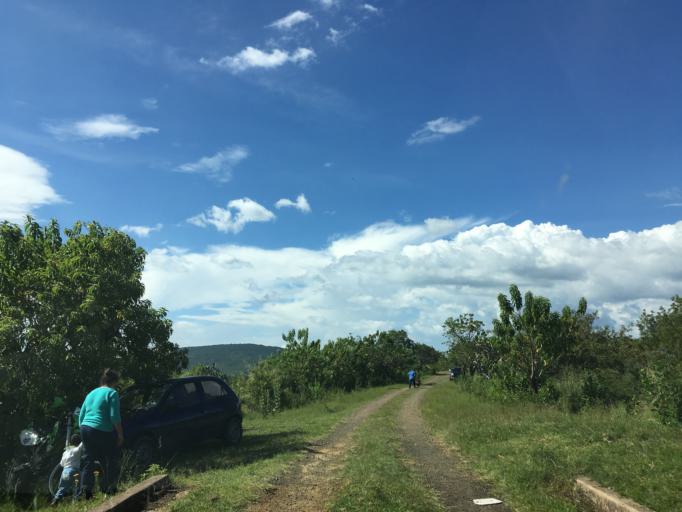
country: MX
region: Michoacan
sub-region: Jimenez
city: Villa Jimenez
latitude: 19.9057
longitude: -101.7713
